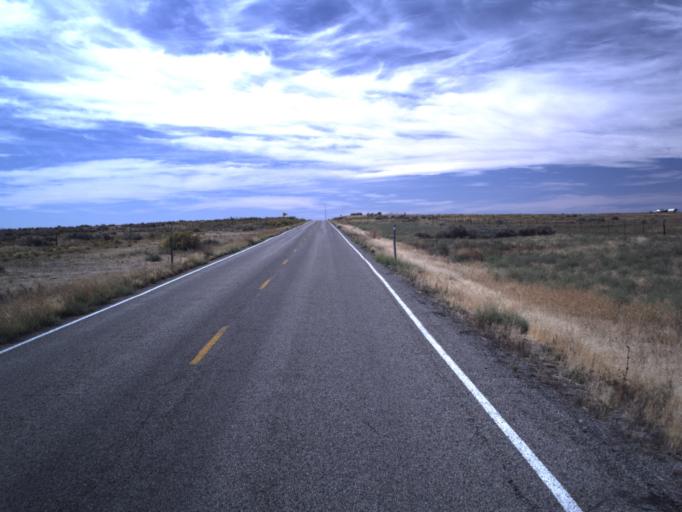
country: US
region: Utah
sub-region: San Juan County
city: Blanding
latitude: 37.3572
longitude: -109.3460
